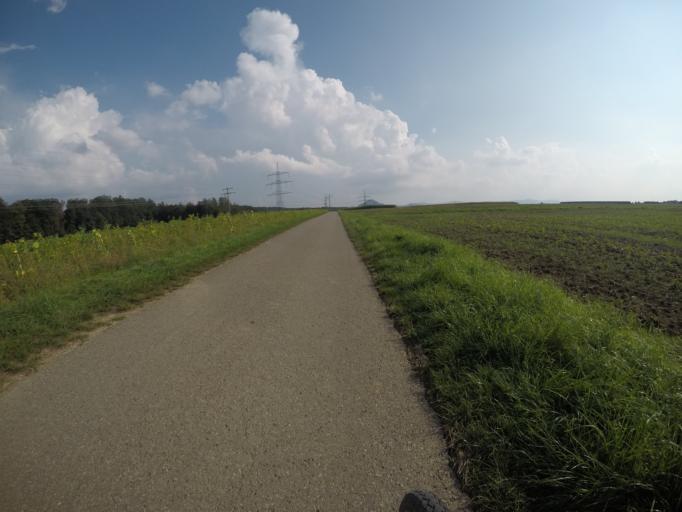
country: DE
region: Baden-Wuerttemberg
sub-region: Tuebingen Region
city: Riederich
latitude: 48.5501
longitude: 9.2385
